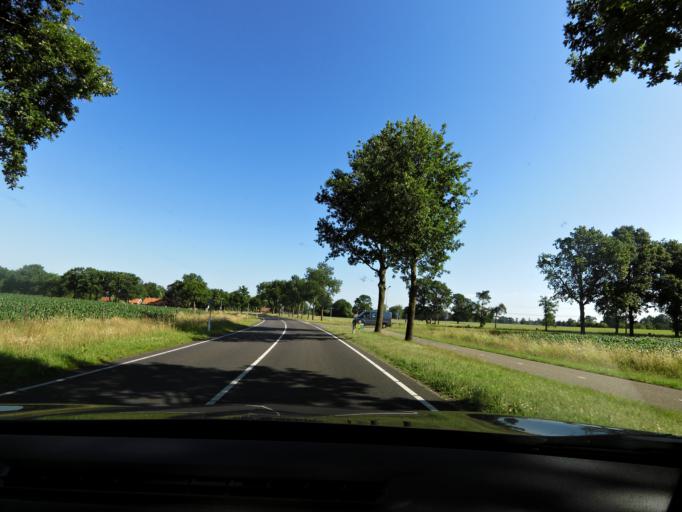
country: NL
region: Overijssel
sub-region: Gemeente Twenterand
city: Den Ham
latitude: 52.4262
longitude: 6.4443
